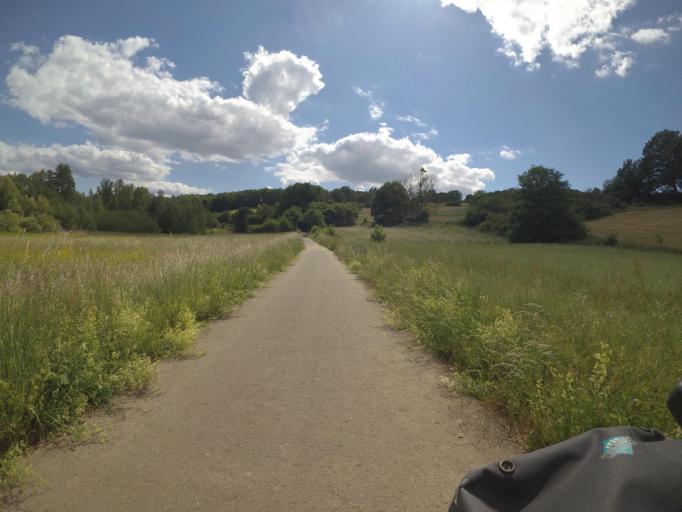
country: DE
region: Rheinland-Pfalz
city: Katzenbach
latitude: 49.6498
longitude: 7.8200
